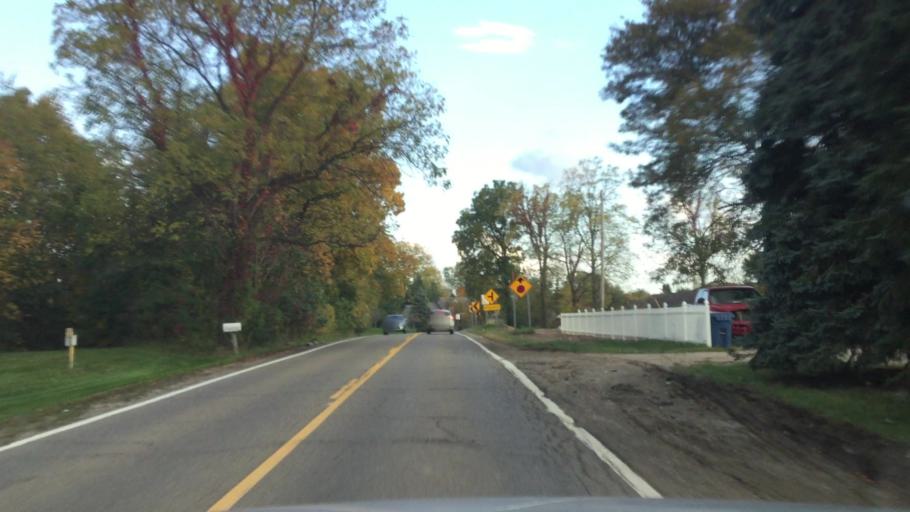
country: US
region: Michigan
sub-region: Oakland County
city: Wolverine Lake
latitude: 42.6430
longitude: -83.4967
